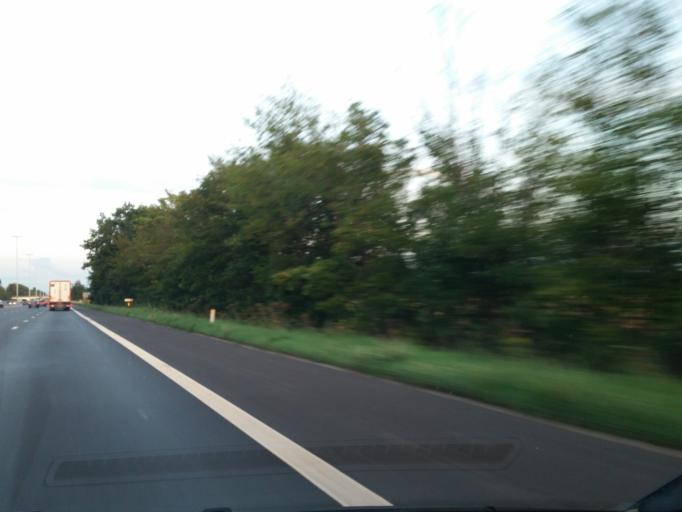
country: BE
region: Flanders
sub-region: Provincie Oost-Vlaanderen
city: Nevele
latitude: 51.0487
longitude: 3.5773
